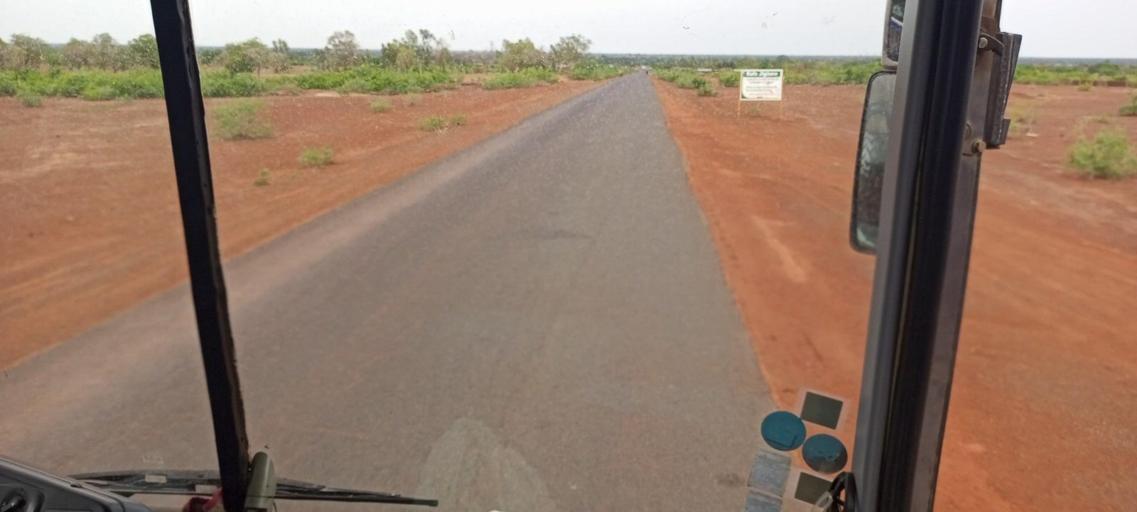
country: ML
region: Segou
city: Bla
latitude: 12.6973
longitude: -5.7239
